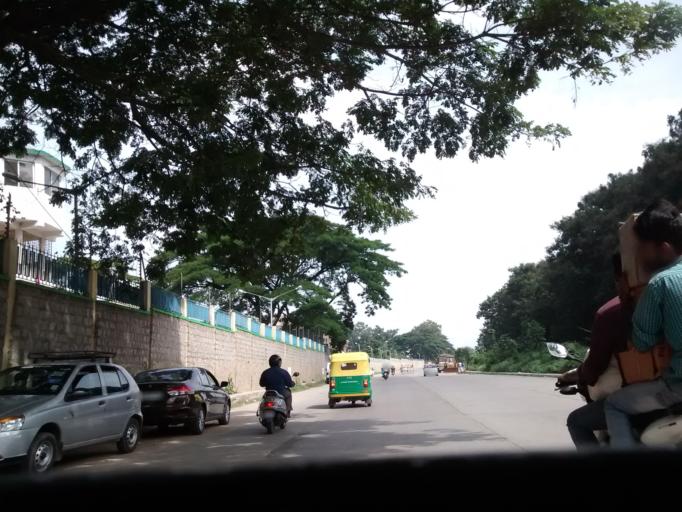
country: IN
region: Karnataka
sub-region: Bangalore Urban
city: Bangalore
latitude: 12.9791
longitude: 77.6525
